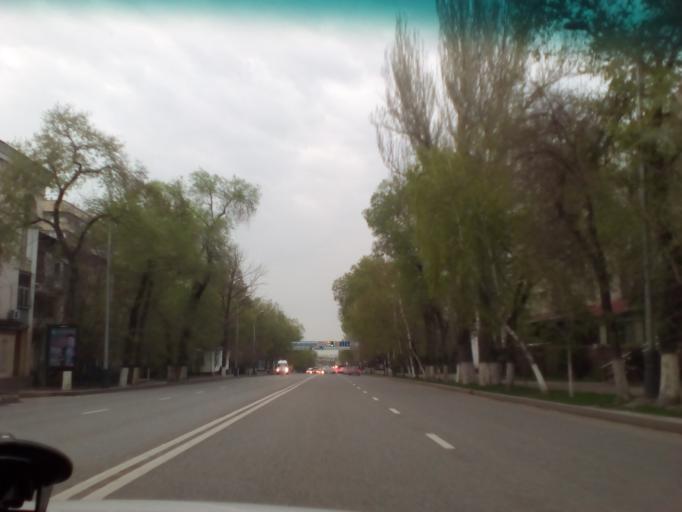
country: KZ
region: Almaty Qalasy
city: Almaty
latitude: 43.2652
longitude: 76.9455
